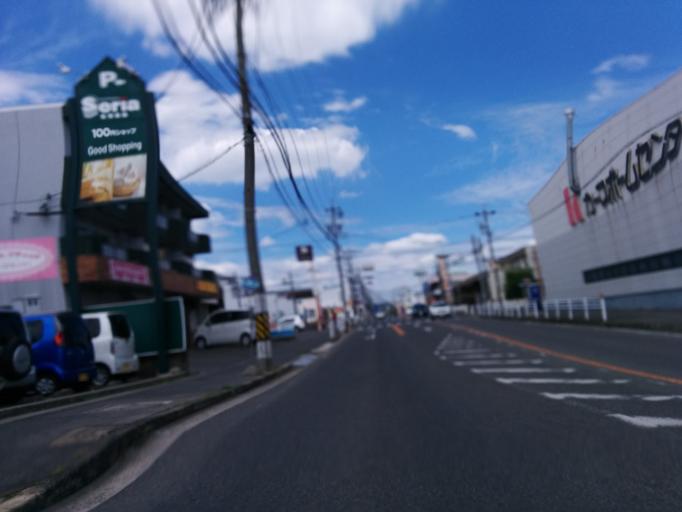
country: JP
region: Aichi
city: Kasugai
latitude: 35.2660
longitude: 136.9831
